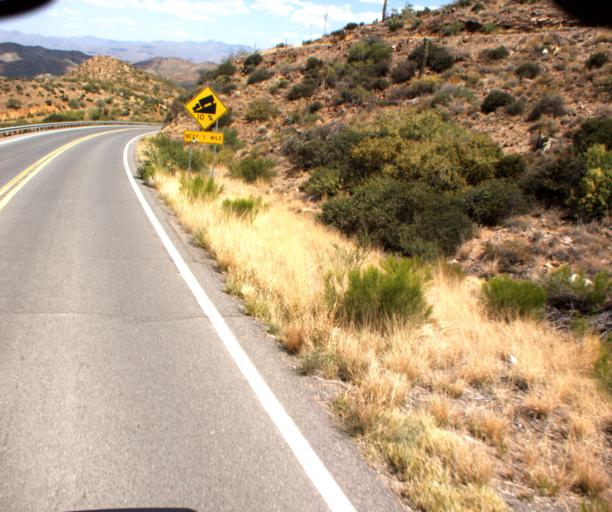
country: US
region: Arizona
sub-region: Pinal County
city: Superior
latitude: 33.2044
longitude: -111.0582
